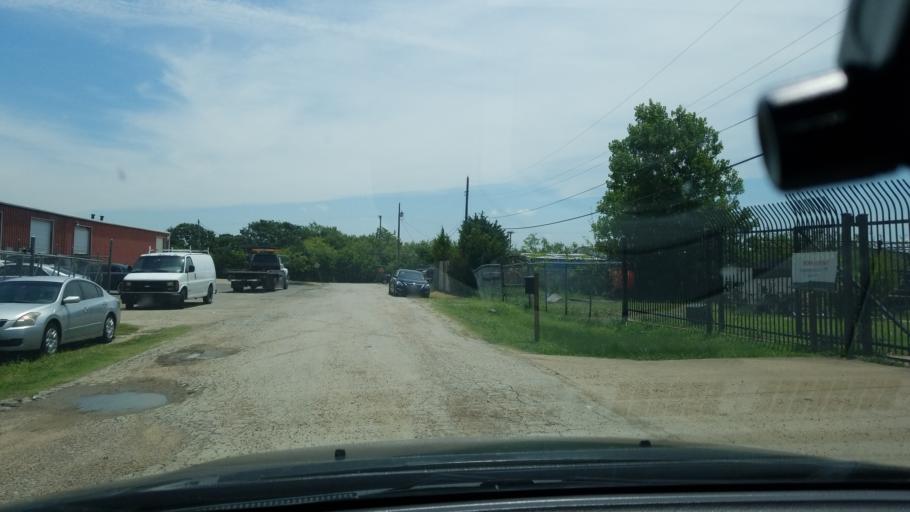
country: US
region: Texas
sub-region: Dallas County
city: Balch Springs
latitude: 32.7426
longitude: -96.6325
